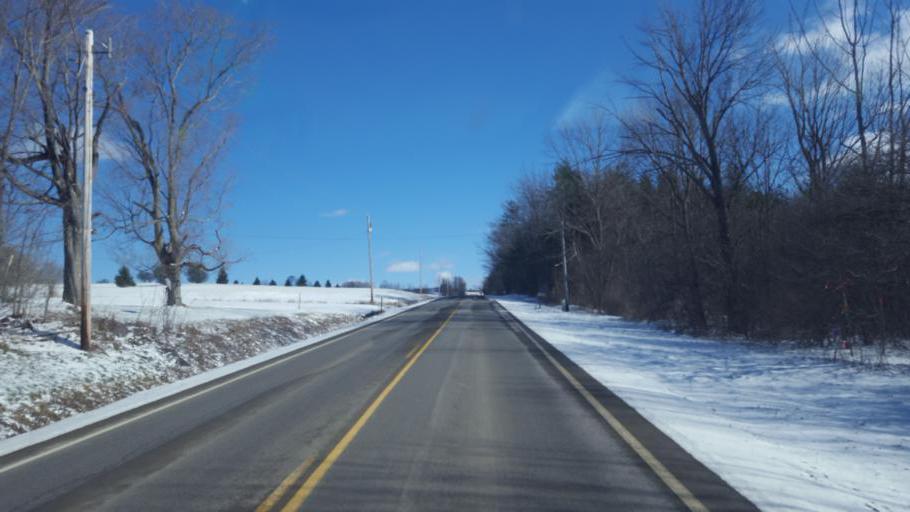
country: US
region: New York
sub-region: Allegany County
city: Friendship
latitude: 42.1990
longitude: -78.1049
